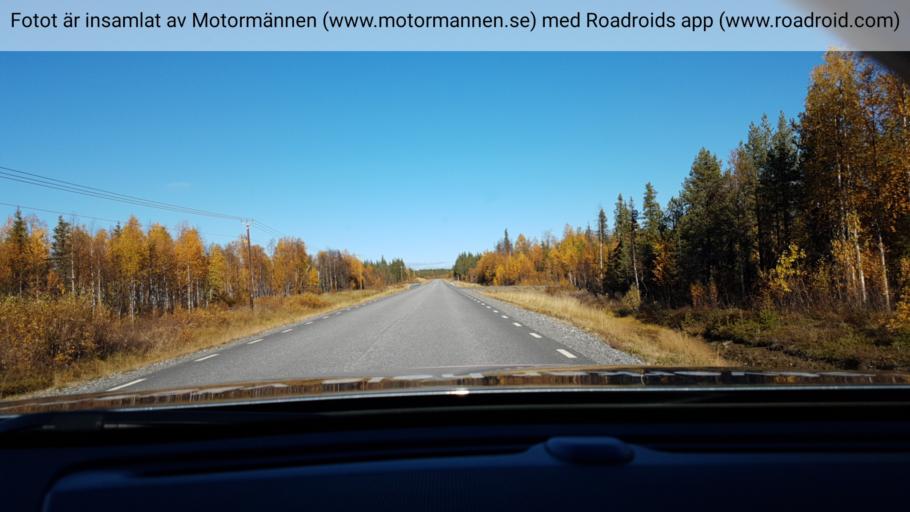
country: SE
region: Norrbotten
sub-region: Gallivare Kommun
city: Gaellivare
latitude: 66.7937
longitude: 21.0384
